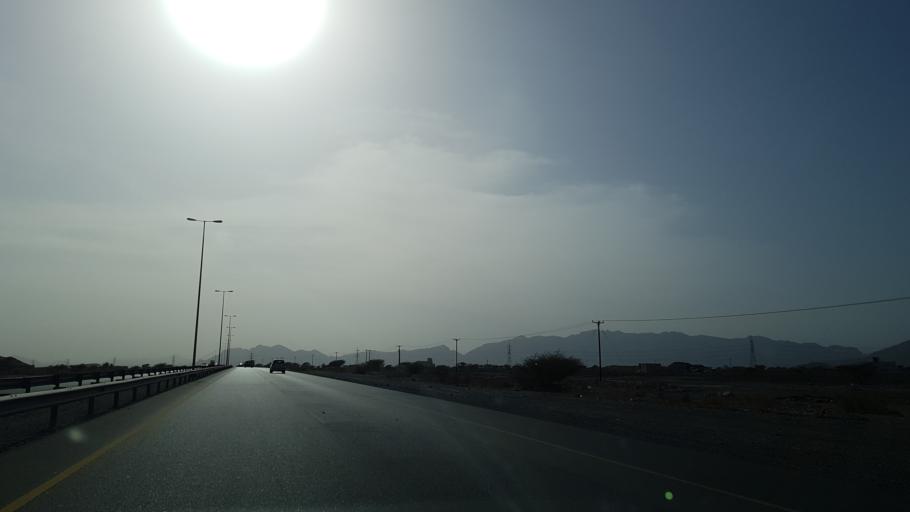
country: OM
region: Muhafazat ad Dakhiliyah
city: Izki
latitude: 22.8916
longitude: 57.6630
